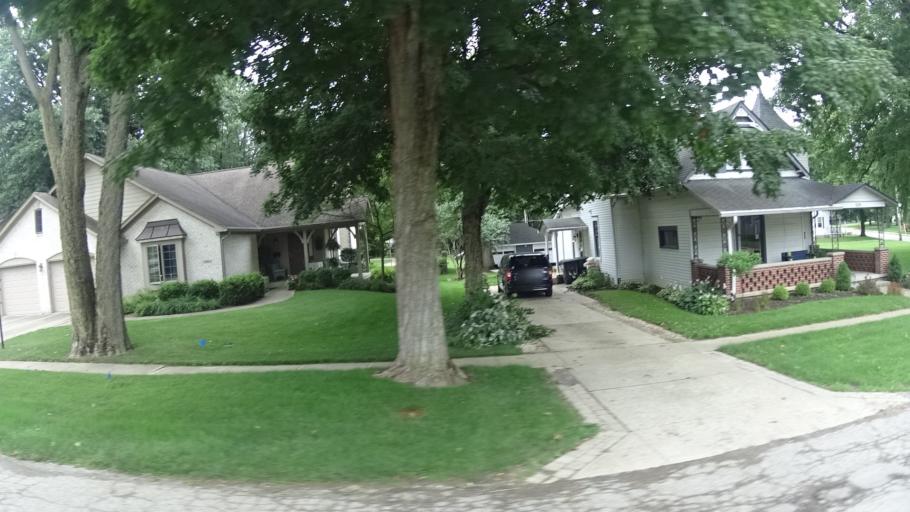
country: US
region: Indiana
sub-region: Madison County
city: Pendleton
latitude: 39.9962
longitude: -85.7443
